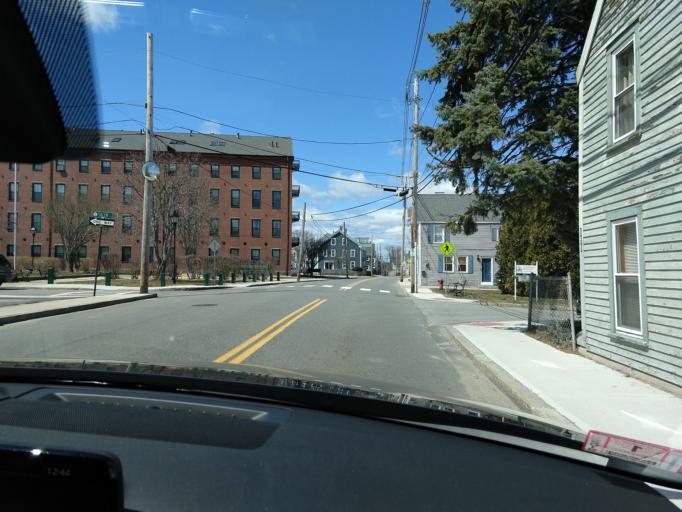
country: US
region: Massachusetts
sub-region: Essex County
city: Newburyport
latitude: 42.8086
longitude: -70.8618
